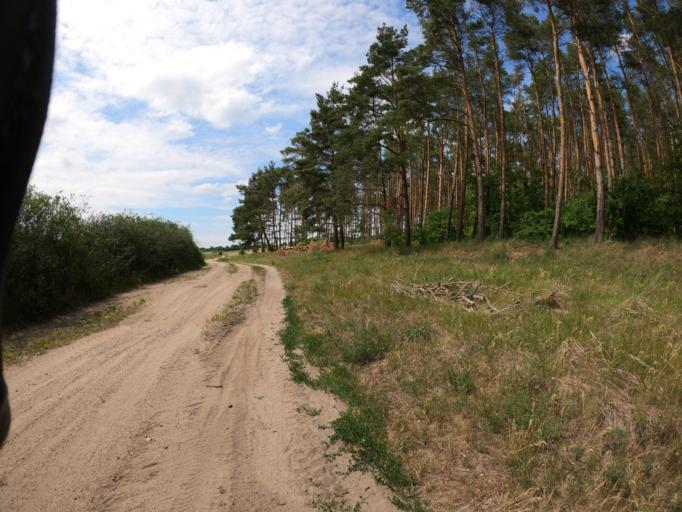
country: DE
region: Brandenburg
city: Letschin
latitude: 52.7321
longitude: 14.3983
